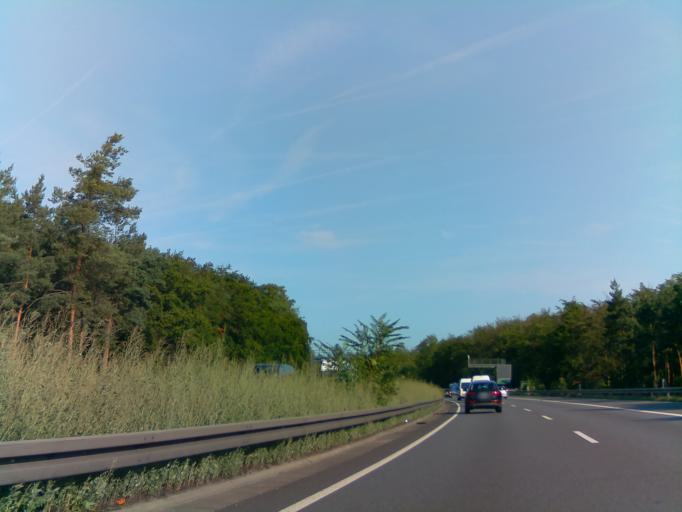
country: DE
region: Hesse
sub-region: Regierungsbezirk Darmstadt
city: Darmstadt
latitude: 49.8365
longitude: 8.6327
